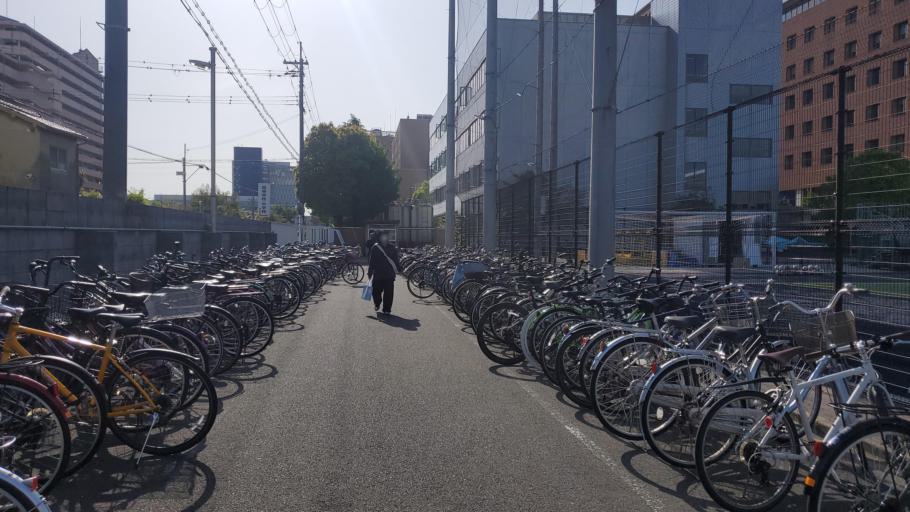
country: JP
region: Osaka
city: Yao
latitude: 34.6506
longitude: 135.5923
